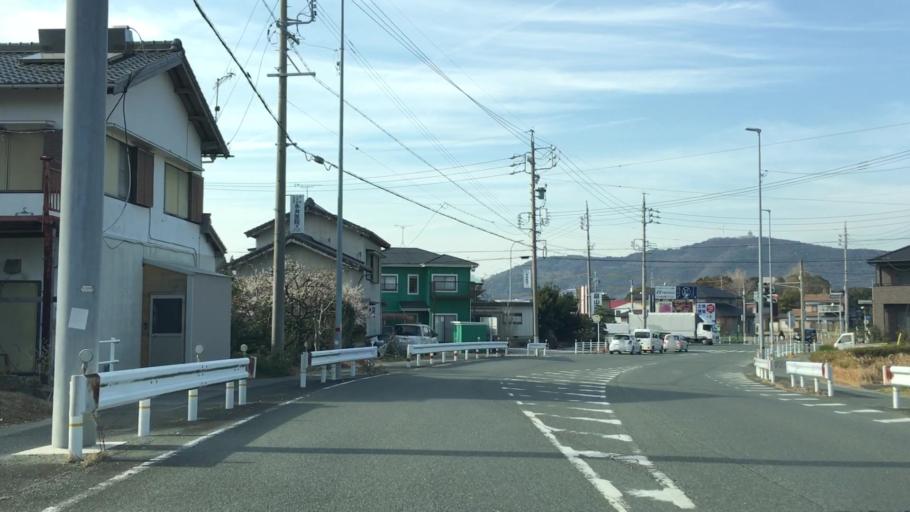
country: JP
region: Aichi
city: Tahara
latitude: 34.6622
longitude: 137.2776
